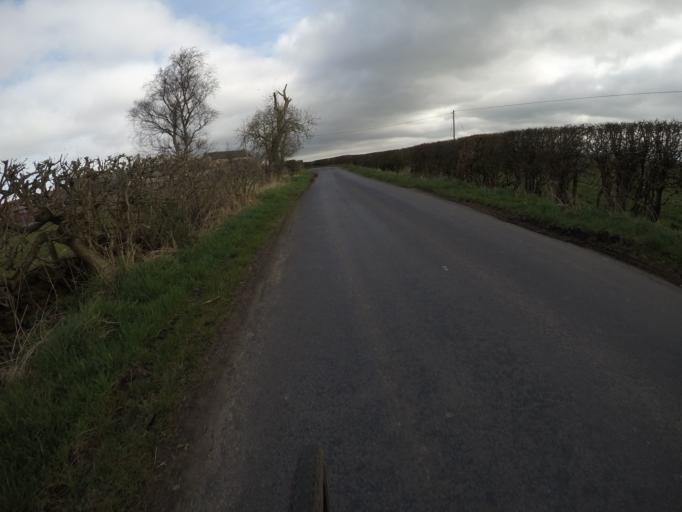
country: GB
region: Scotland
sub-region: North Ayrshire
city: Springside
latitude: 55.6631
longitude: -4.6033
